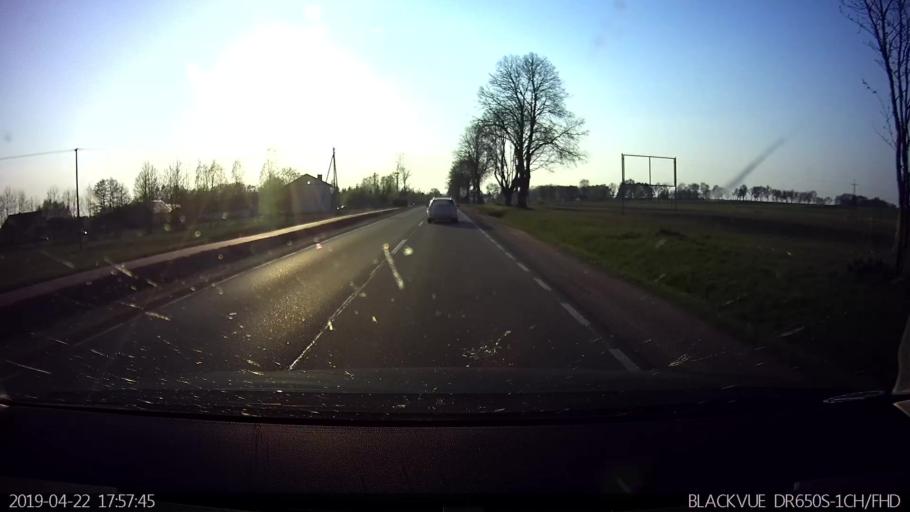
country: PL
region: Masovian Voivodeship
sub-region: Powiat wegrowski
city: Korytnica
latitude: 52.4701
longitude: 21.8865
